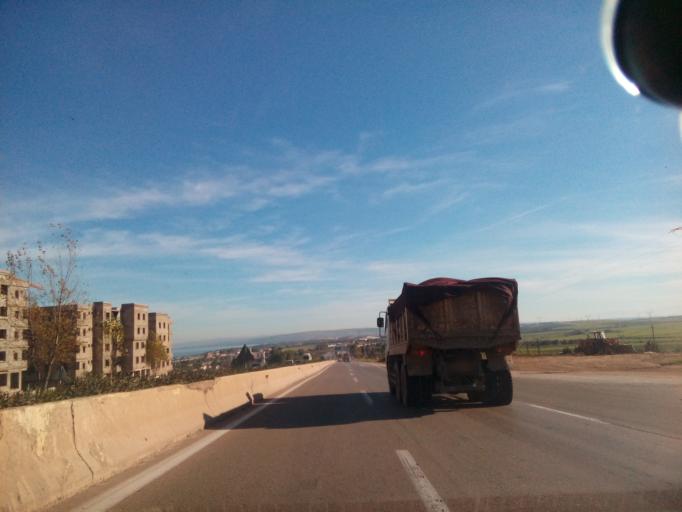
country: DZ
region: Oran
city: Ain el Bya
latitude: 35.7866
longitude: -0.1731
